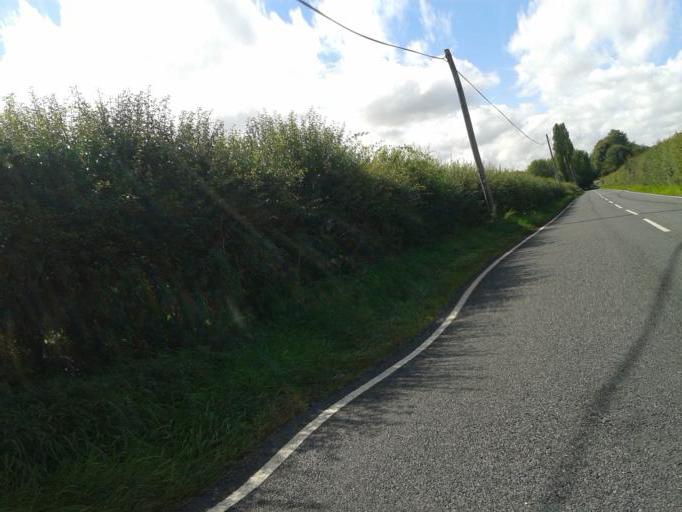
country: GB
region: England
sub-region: Cambridgeshire
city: Duxford
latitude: 52.0208
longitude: 0.1401
